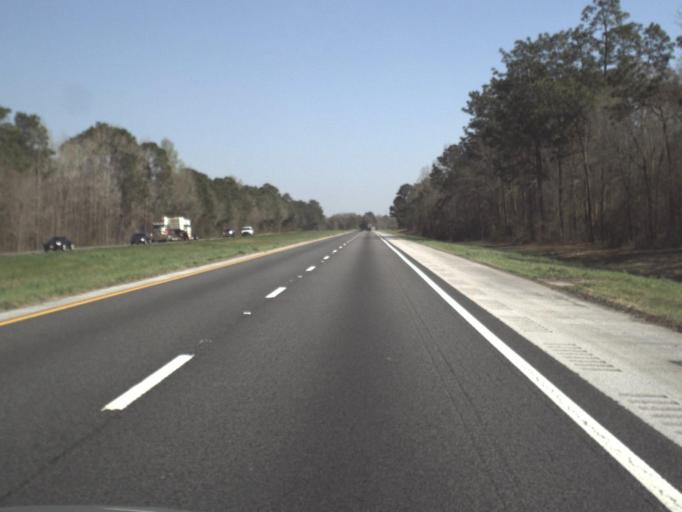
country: US
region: Florida
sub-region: Jackson County
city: Marianna
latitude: 30.6814
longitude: -85.0942
